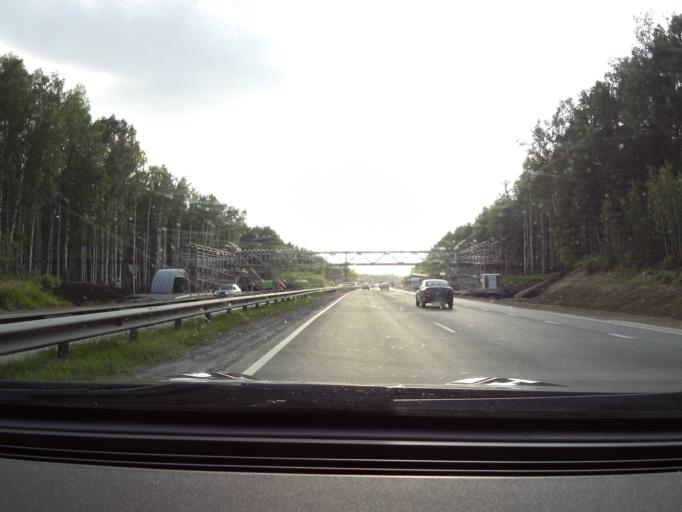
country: RU
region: Sverdlovsk
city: Talitsa
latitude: 56.8387
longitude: 60.1198
